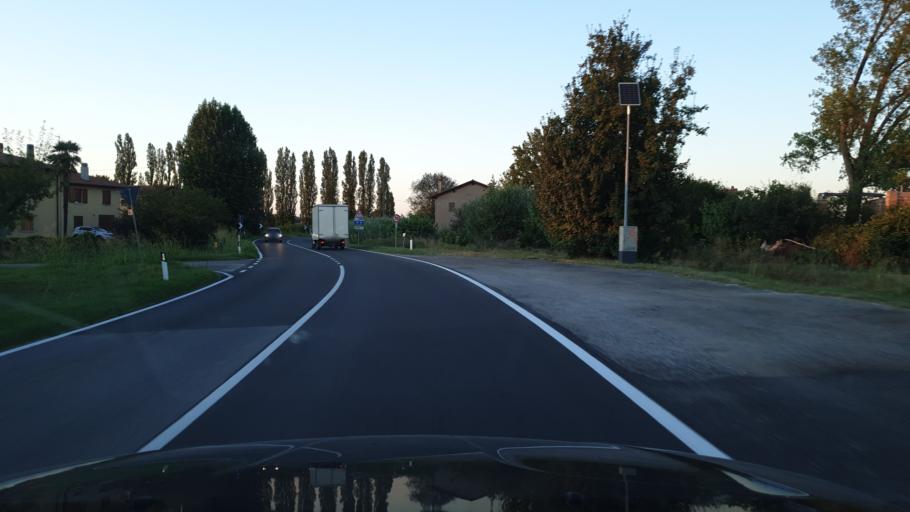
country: IT
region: Emilia-Romagna
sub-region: Provincia di Bologna
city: Progresso
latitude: 44.5715
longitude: 11.4049
